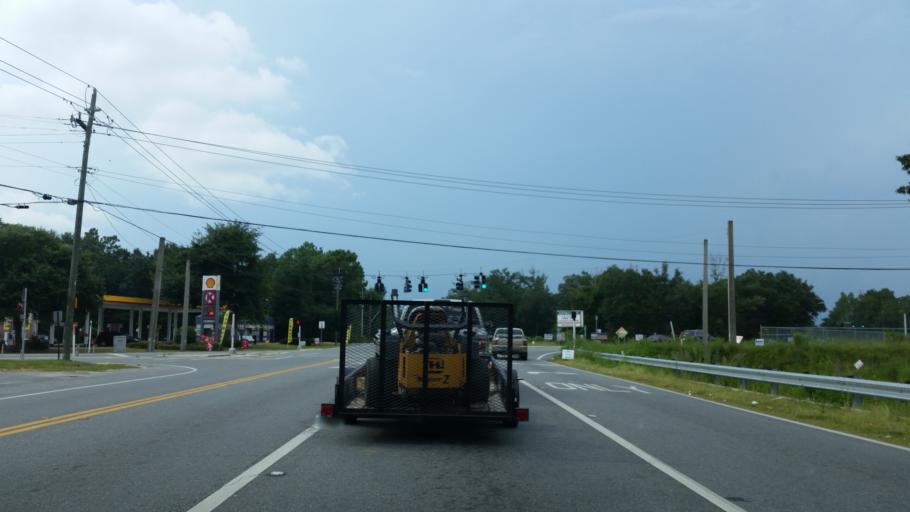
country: US
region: Florida
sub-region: Santa Rosa County
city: Wallace
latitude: 30.6427
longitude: -87.1800
